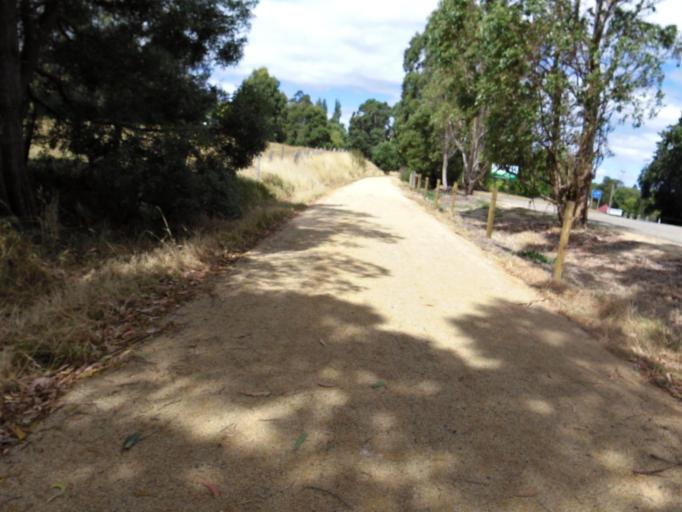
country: AU
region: Victoria
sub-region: Bass Coast
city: North Wonthaggi
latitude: -38.4252
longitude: 145.8176
